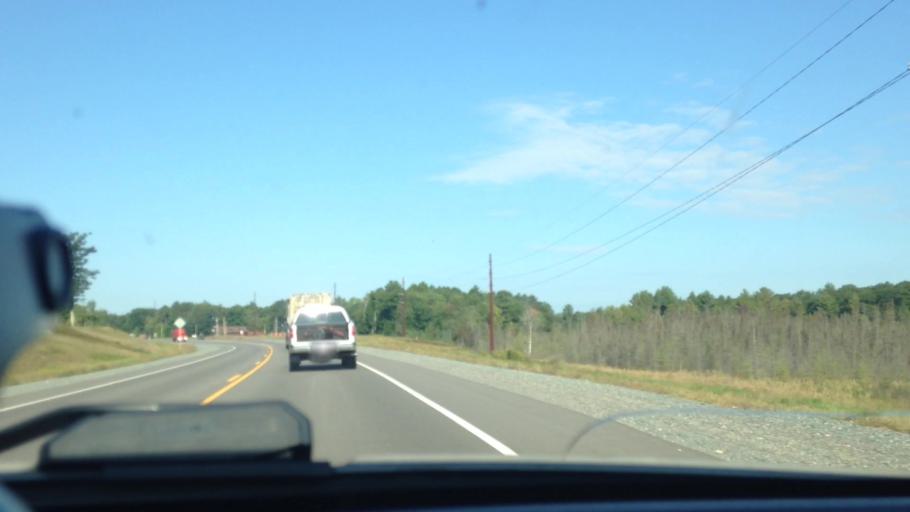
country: US
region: Michigan
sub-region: Dickinson County
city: Iron Mountain
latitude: 45.8798
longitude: -88.1245
